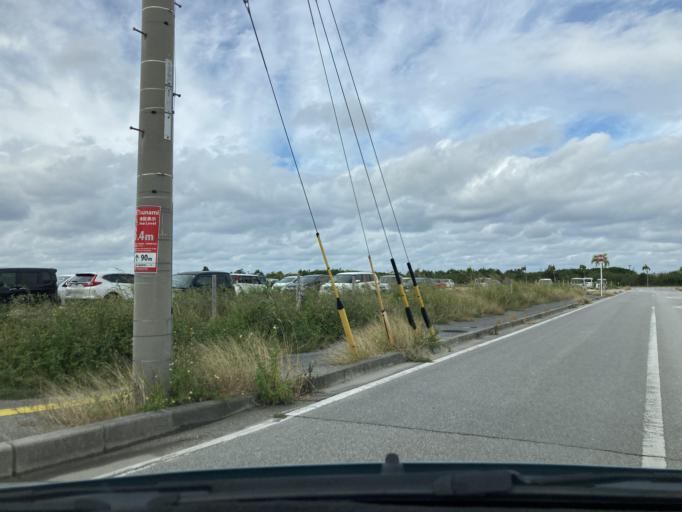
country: JP
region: Okinawa
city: Itoman
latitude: 26.1590
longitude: 127.6521
